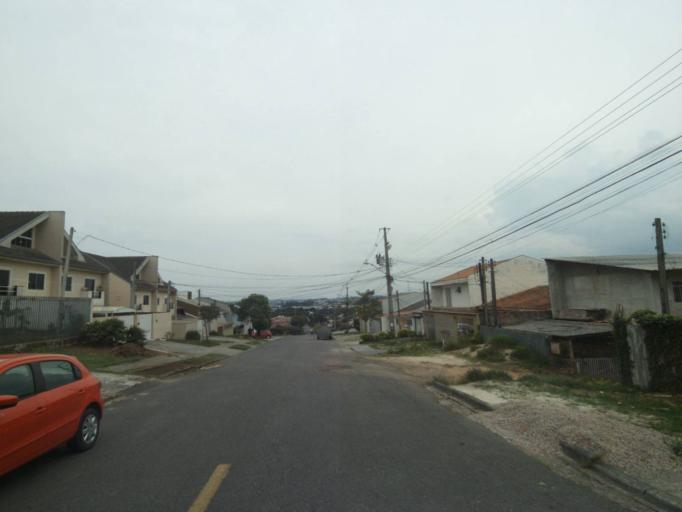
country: BR
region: Parana
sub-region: Pinhais
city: Pinhais
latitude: -25.4178
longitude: -49.2036
